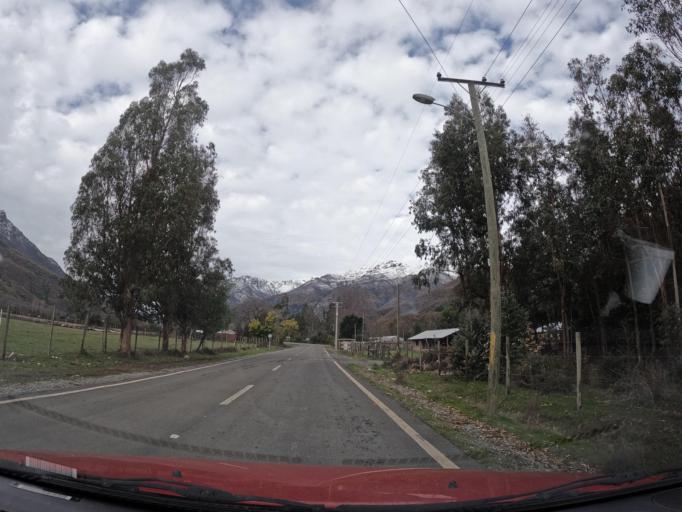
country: CL
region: Maule
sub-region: Provincia de Linares
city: Colbun
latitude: -35.8609
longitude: -71.2589
